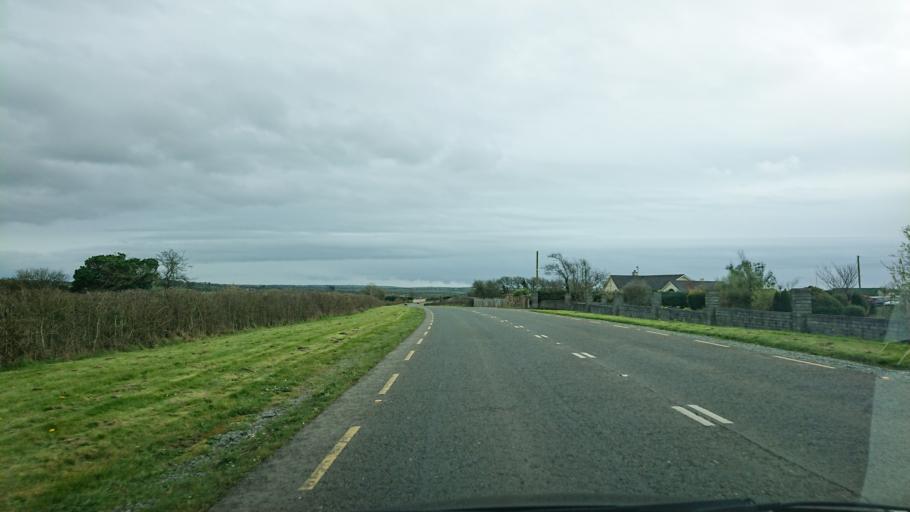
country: IE
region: Munster
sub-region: Waterford
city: Waterford
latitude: 52.2000
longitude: -7.0801
